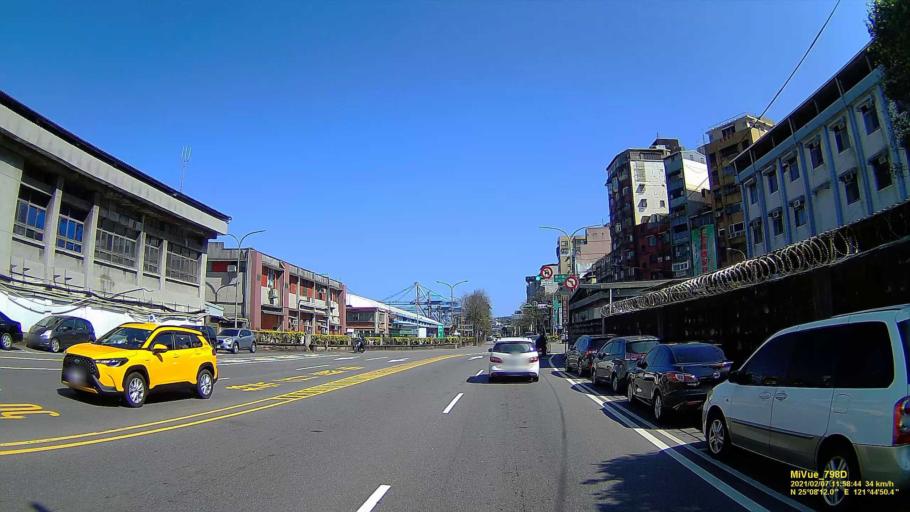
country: TW
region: Taiwan
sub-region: Keelung
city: Keelung
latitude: 25.1372
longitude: 121.7473
